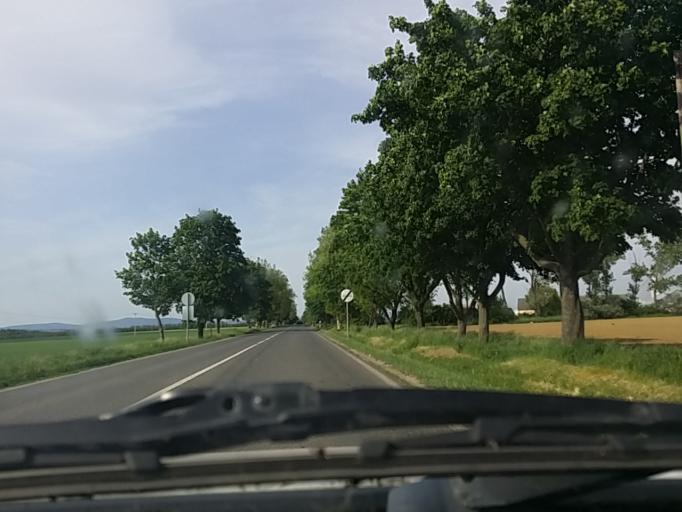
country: HU
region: Baranya
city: Harkany
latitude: 45.9189
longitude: 18.2330
